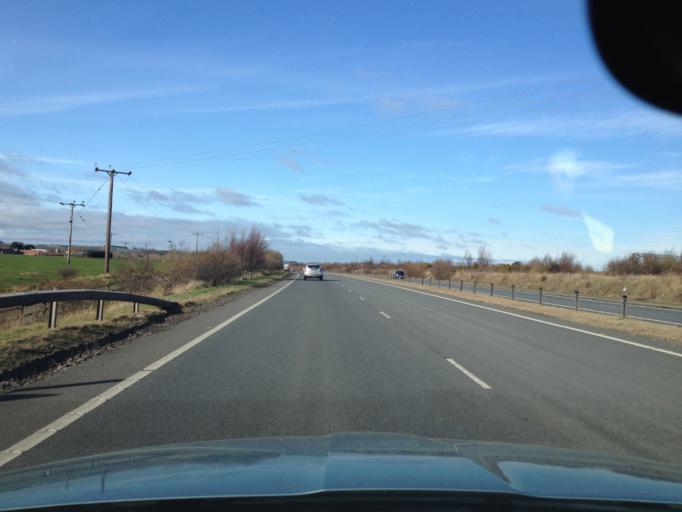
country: GB
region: Scotland
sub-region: East Lothian
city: Dunbar
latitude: 55.9886
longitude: -2.5694
